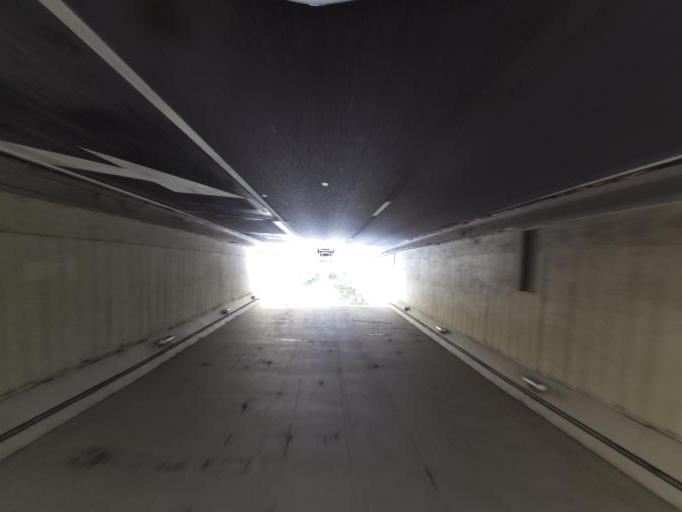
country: BE
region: Wallonia
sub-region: Province du Hainaut
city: Mons
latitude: 50.4606
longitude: 3.9567
